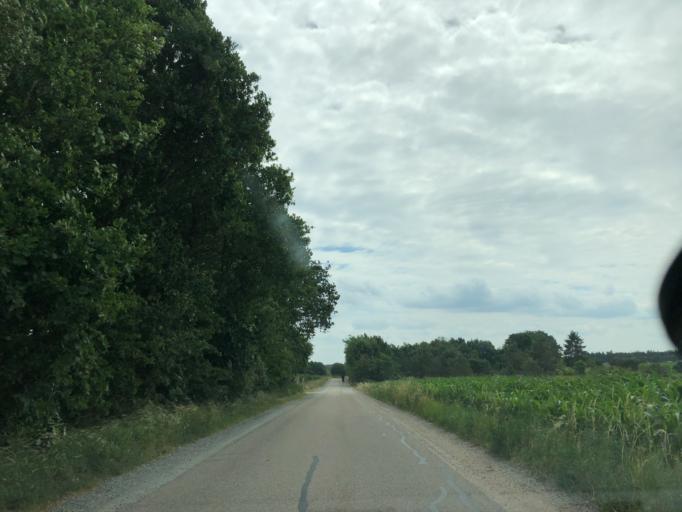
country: DK
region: Central Jutland
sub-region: Silkeborg Kommune
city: Svejbaek
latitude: 56.2055
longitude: 9.6892
